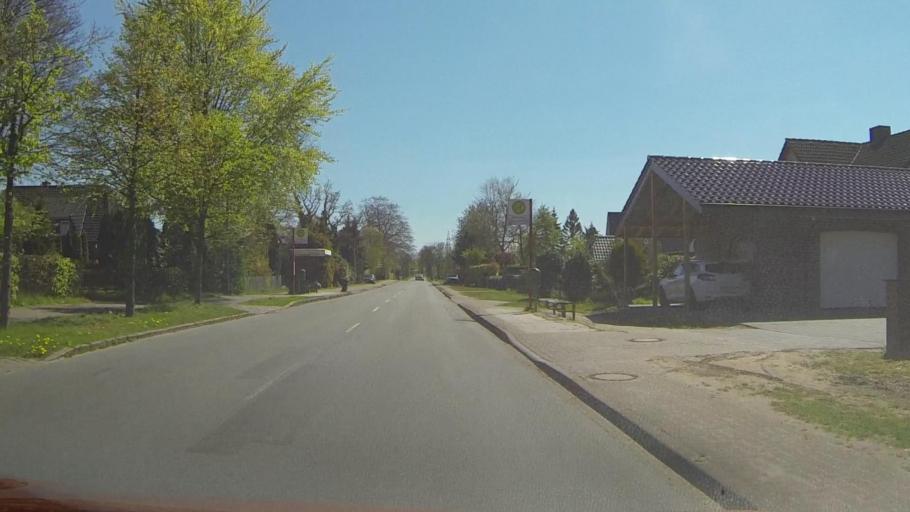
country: DE
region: Schleswig-Holstein
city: Ellerbek
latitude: 53.6564
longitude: 9.8696
